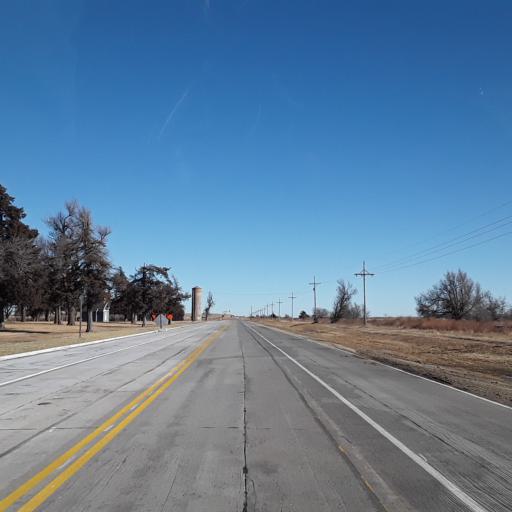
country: US
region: Kansas
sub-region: Pawnee County
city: Larned
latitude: 38.0774
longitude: -99.2405
